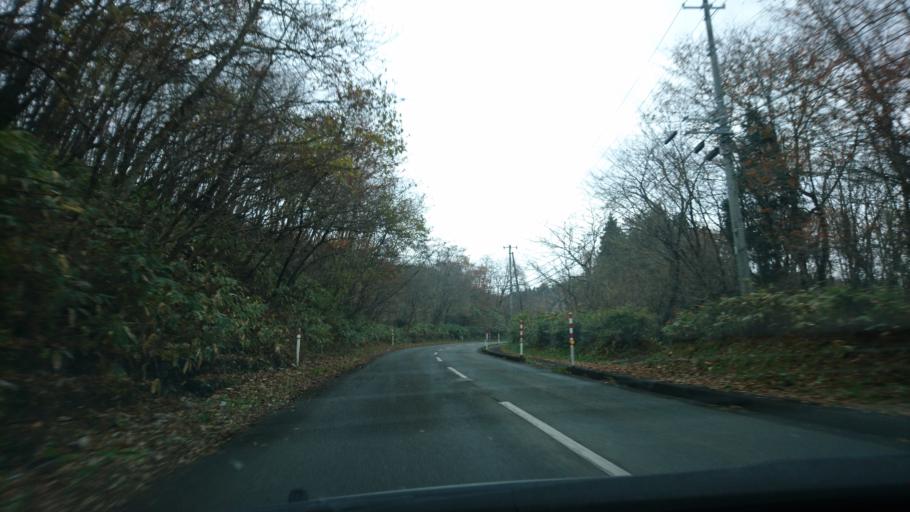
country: JP
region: Iwate
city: Ichinoseki
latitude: 38.9665
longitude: 140.9389
